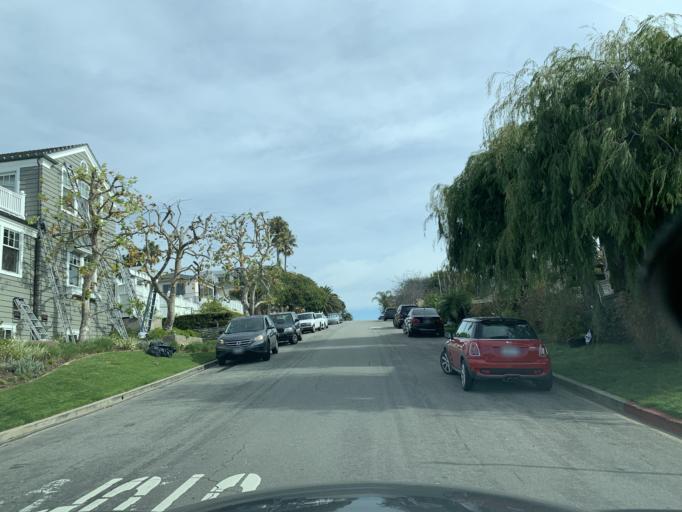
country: US
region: California
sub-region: Los Angeles County
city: Manhattan Beach
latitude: 33.8838
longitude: -118.4033
